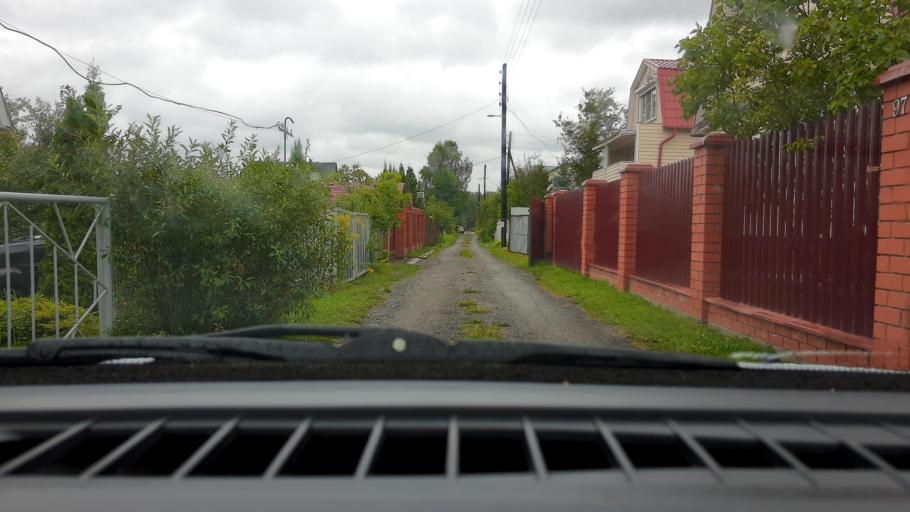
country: RU
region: Nizjnij Novgorod
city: Babino
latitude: 56.1521
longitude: 43.6346
